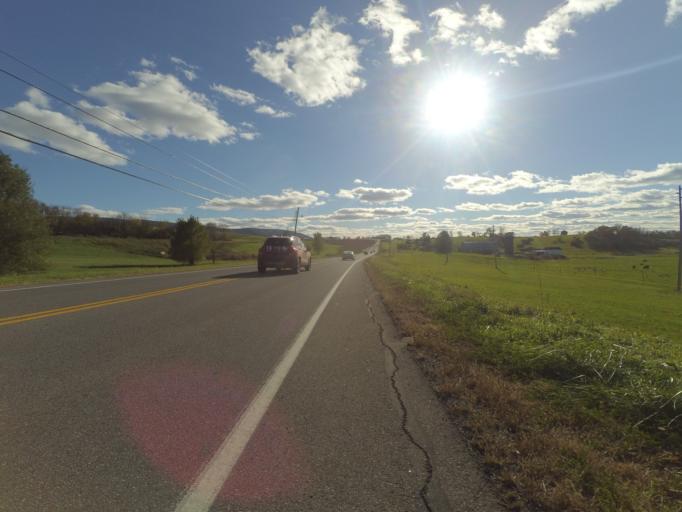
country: US
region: Pennsylvania
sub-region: Centre County
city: Pleasant Gap
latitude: 40.8628
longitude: -77.7821
